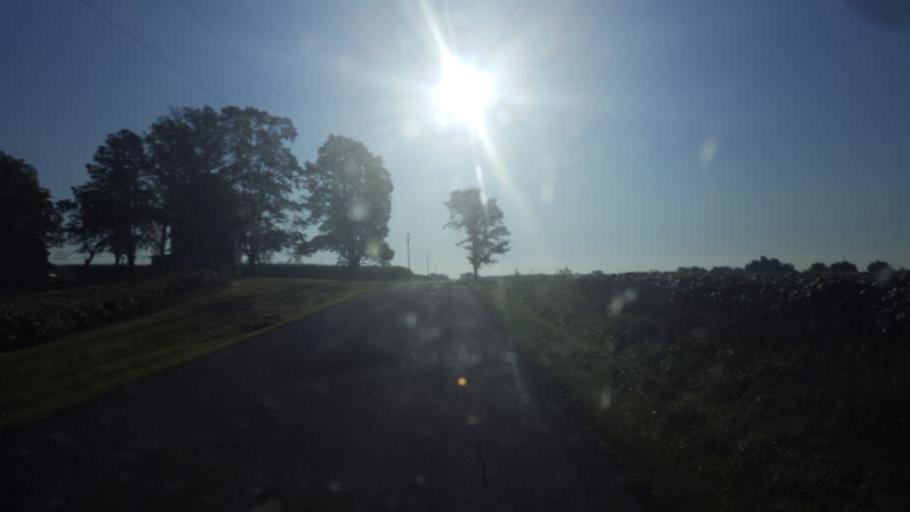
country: US
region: Ohio
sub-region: Morrow County
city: Mount Gilead
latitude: 40.5390
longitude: -82.7697
